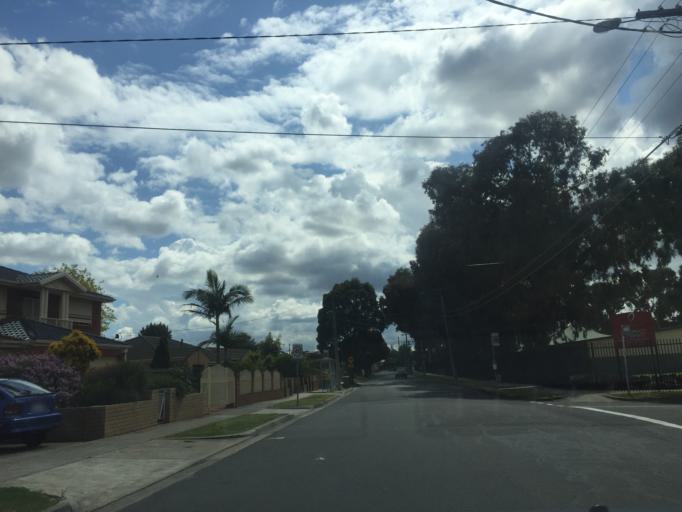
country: AU
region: Victoria
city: Heidelberg West
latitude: -37.7346
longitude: 145.0287
